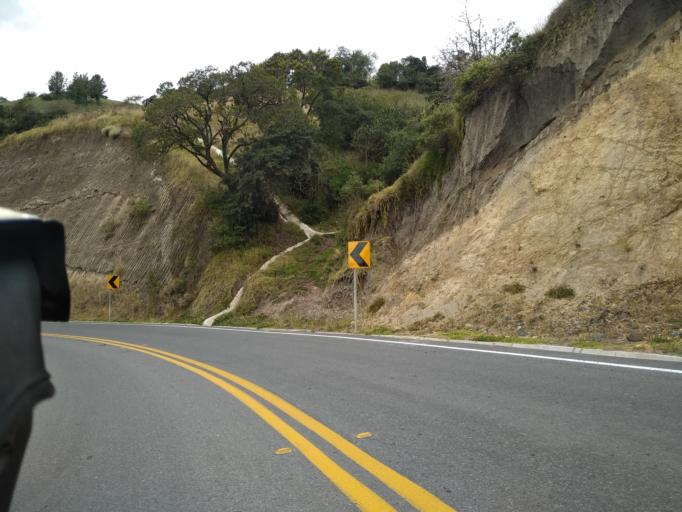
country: EC
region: Cotopaxi
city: Saquisili
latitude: -0.7598
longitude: -78.9120
